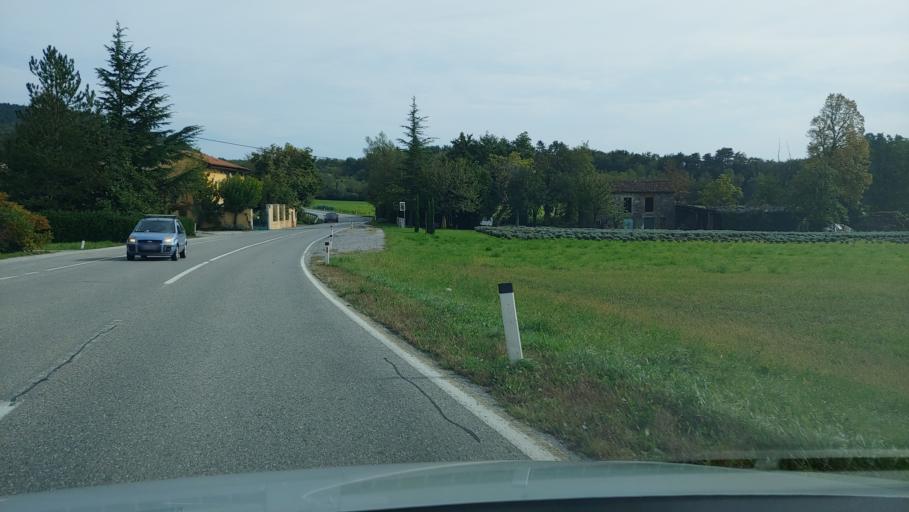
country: SI
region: Nova Gorica
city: Sempas
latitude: 45.9199
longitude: 13.7577
